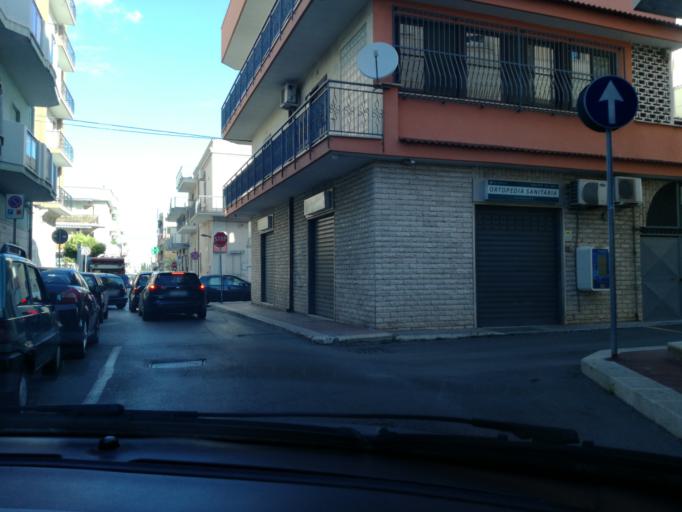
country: IT
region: Apulia
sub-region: Provincia di Bari
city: Triggiano
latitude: 41.0640
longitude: 16.9187
